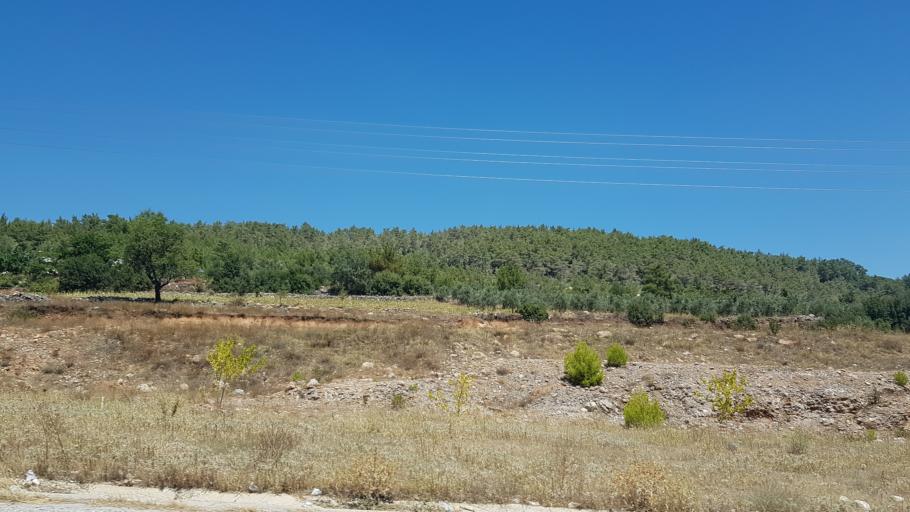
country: TR
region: Mugla
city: Turgut
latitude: 37.3077
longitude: 28.0243
